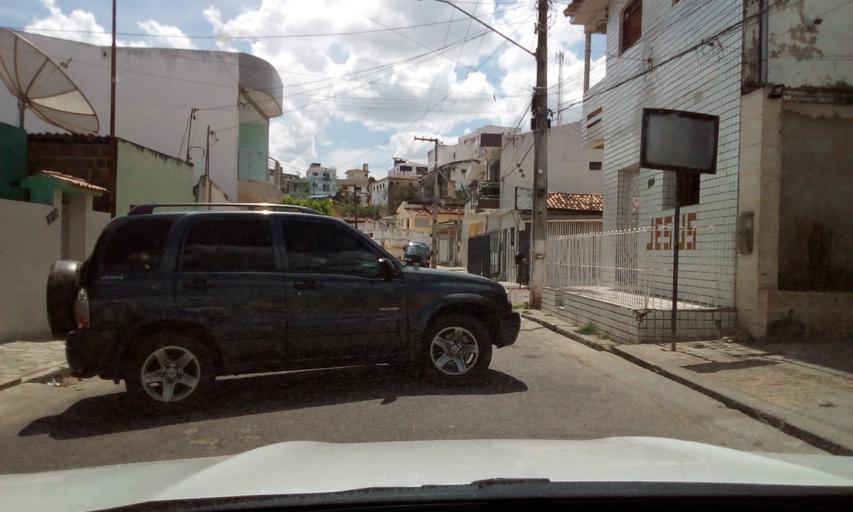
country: BR
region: Paraiba
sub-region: Guarabira
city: Guarabira
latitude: -6.8488
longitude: -35.4874
